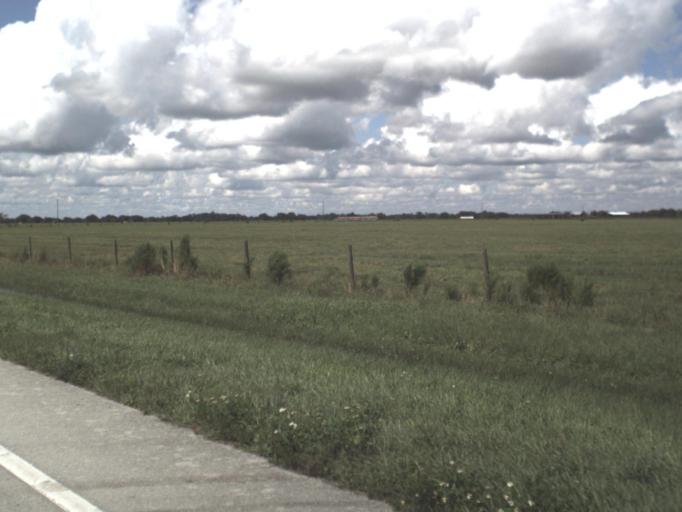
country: US
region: Florida
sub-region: DeSoto County
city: Arcadia
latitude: 27.2429
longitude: -81.9461
